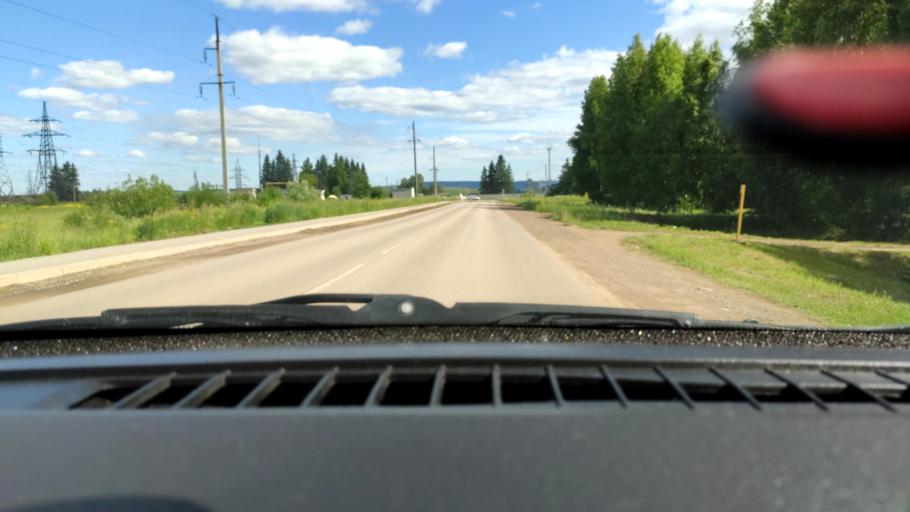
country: RU
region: Perm
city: Kultayevo
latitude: 57.8896
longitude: 55.9217
